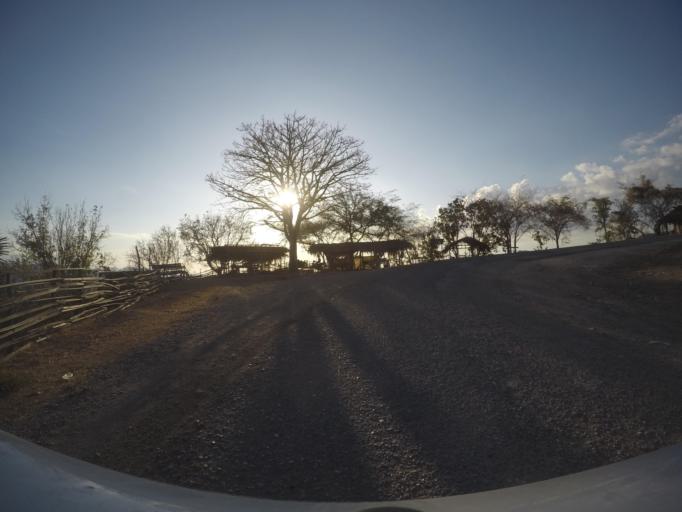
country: ID
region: East Nusa Tenggara
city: Atambua
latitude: -8.9633
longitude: 125.0213
